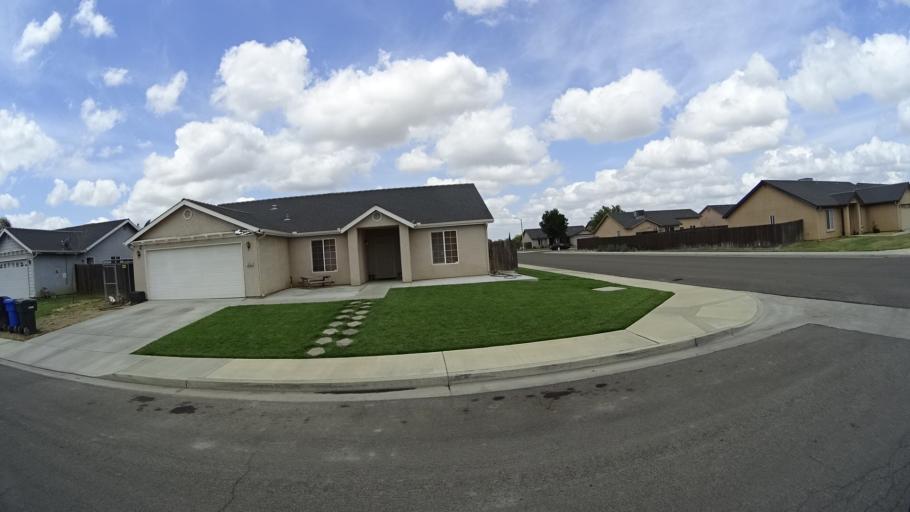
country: US
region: California
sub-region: Kings County
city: Home Garden
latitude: 36.3002
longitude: -119.6584
